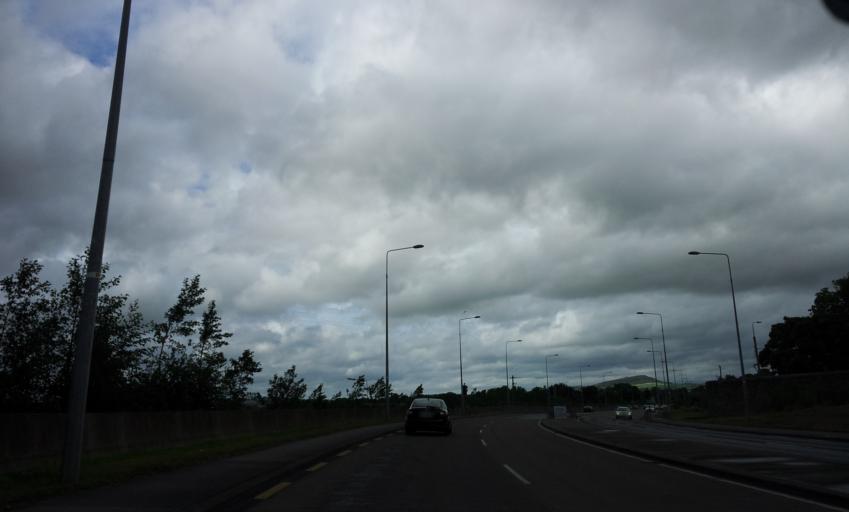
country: IE
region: Munster
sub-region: Waterford
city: Waterford
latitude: 52.2714
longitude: -7.1329
